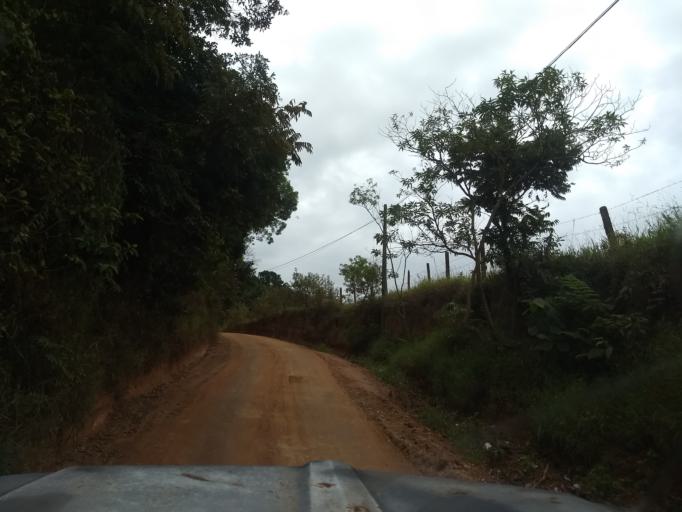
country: BR
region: Sao Paulo
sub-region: Cabreuva
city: Cabreuva
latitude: -23.3999
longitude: -47.1943
